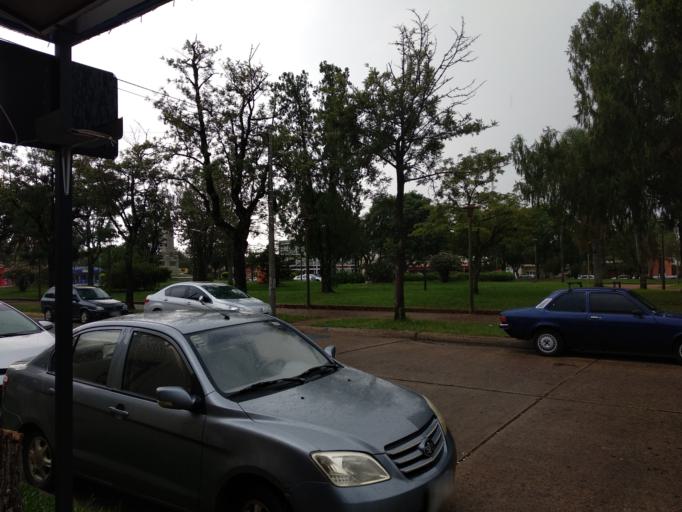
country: UY
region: Artigas
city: Artigas
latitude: -30.4050
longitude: -56.4689
